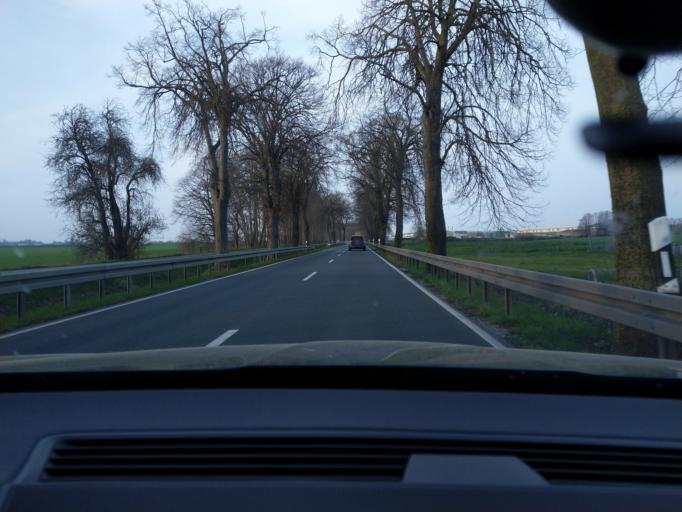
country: DE
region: Mecklenburg-Vorpommern
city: Wendorf
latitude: 54.2828
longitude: 13.0474
